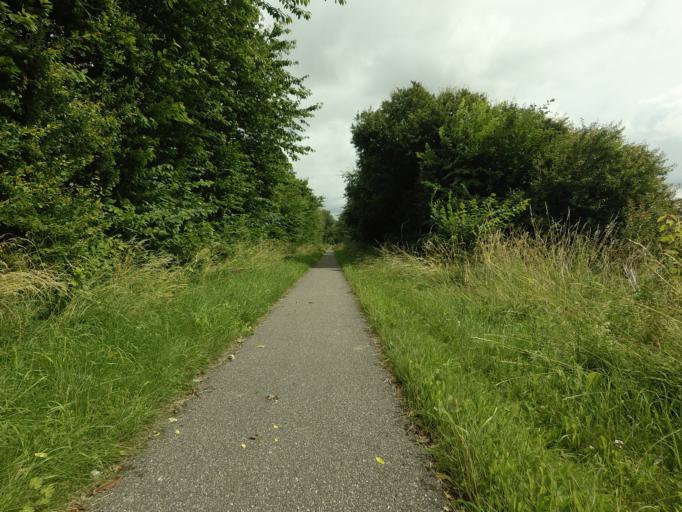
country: DK
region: Central Jutland
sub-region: Favrskov Kommune
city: Hammel
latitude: 56.3213
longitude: 9.8758
